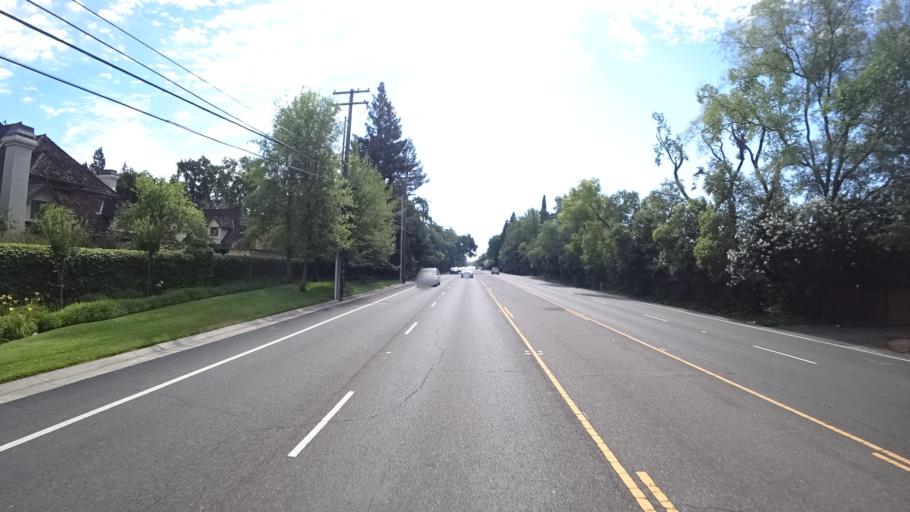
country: US
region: California
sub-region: Sacramento County
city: Arden-Arcade
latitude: 38.5742
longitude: -121.3991
